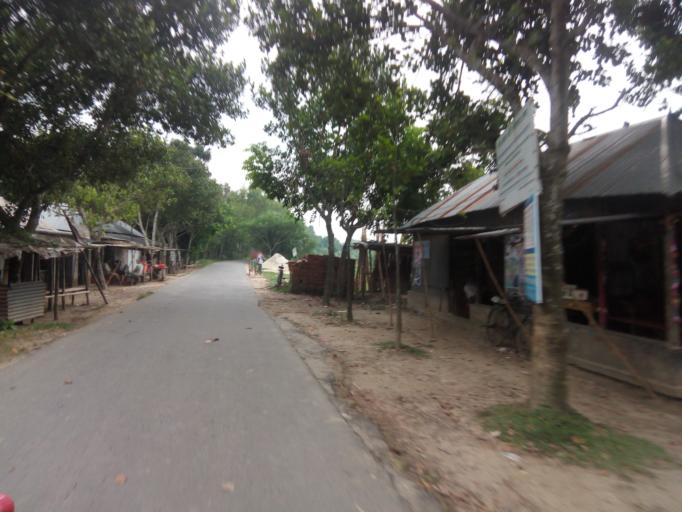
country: BD
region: Khulna
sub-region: Magura
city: Magura
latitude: 23.5063
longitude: 89.6124
